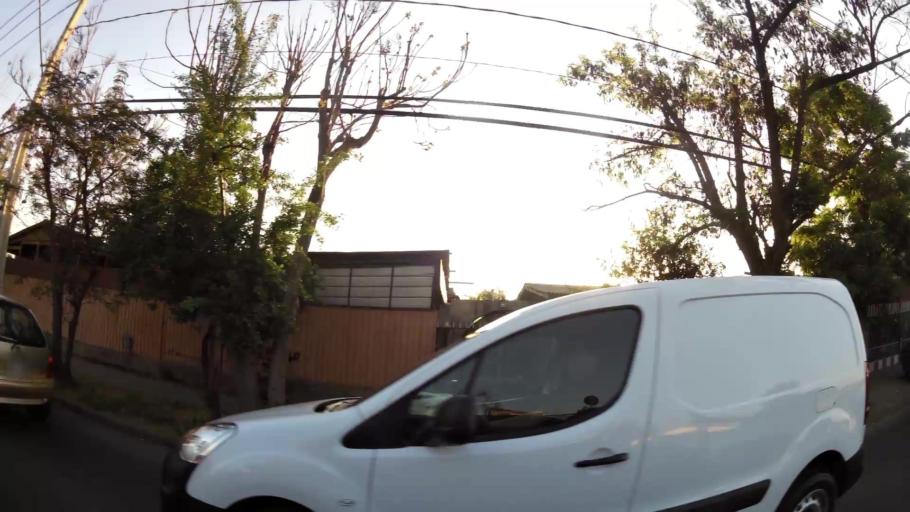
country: CL
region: Santiago Metropolitan
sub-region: Provincia de Santiago
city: Santiago
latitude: -33.5097
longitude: -70.6284
